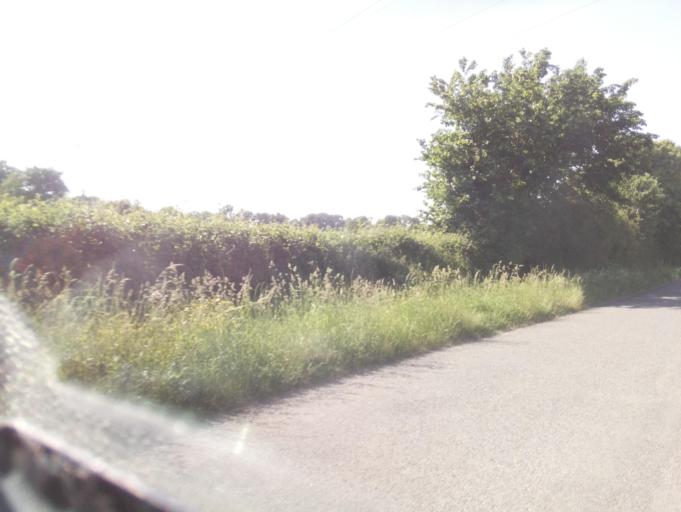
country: GB
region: England
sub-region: Hampshire
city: Abbotts Ann
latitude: 51.2497
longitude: -1.5736
